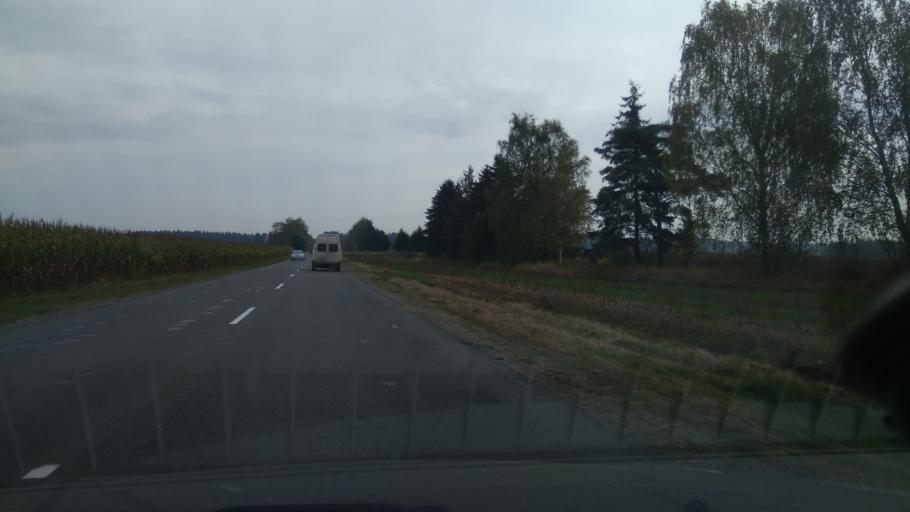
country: BY
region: Minsk
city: Rudzyensk
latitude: 53.6149
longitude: 27.7577
